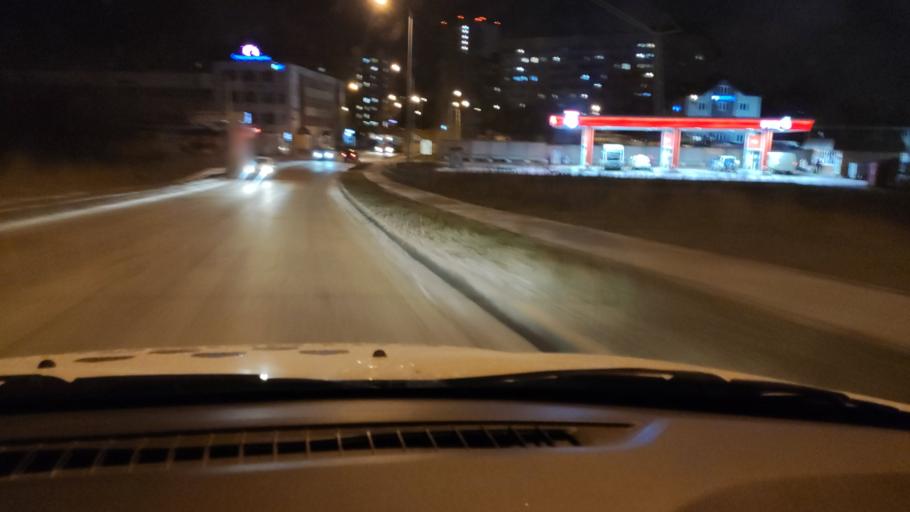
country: RU
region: Perm
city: Perm
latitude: 57.9820
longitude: 56.2805
